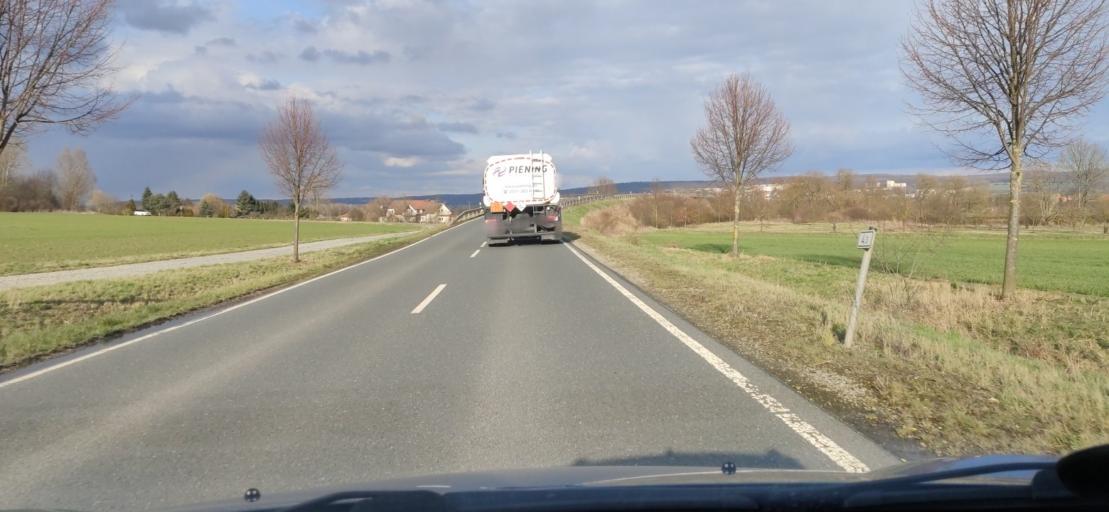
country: DE
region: Lower Saxony
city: Rosdorf
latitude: 51.4943
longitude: 9.9056
